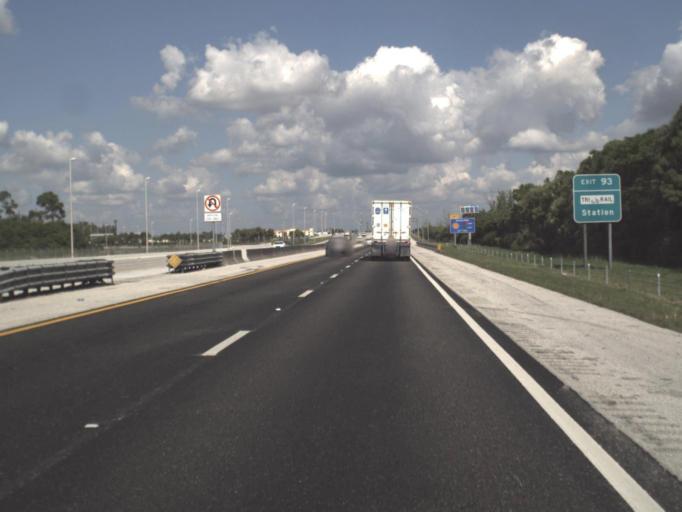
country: US
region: Florida
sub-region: Palm Beach County
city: Greenacres City
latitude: 26.6093
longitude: -80.1735
